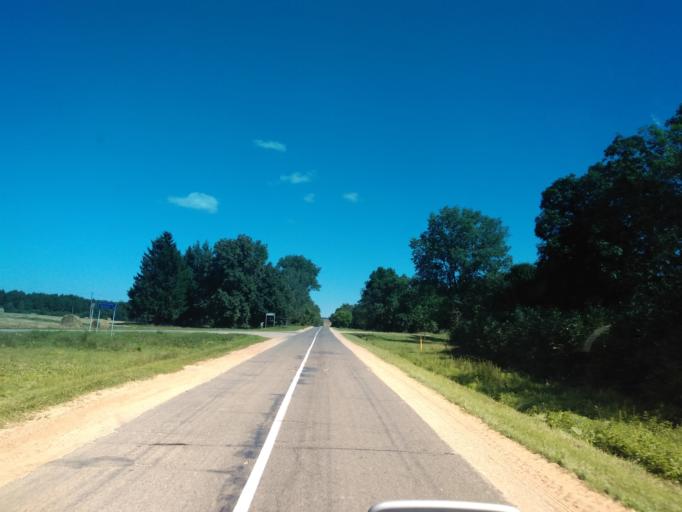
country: BY
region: Minsk
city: Stan'kava
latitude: 53.6334
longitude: 27.2767
